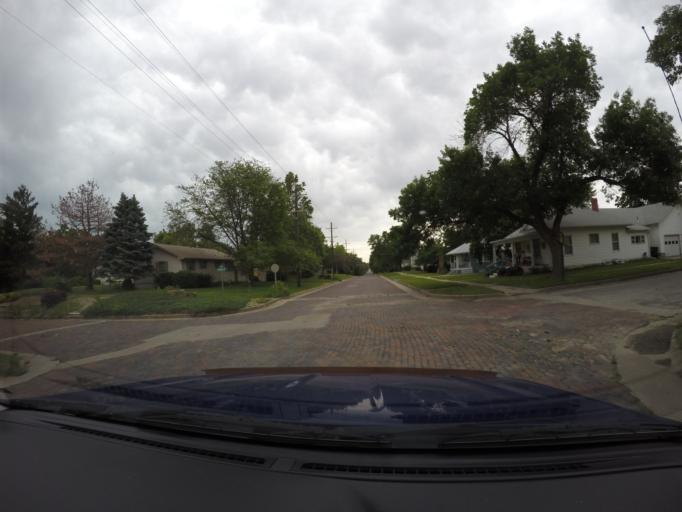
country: US
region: Kansas
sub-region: Clay County
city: Clay Center
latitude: 39.3846
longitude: -97.1304
